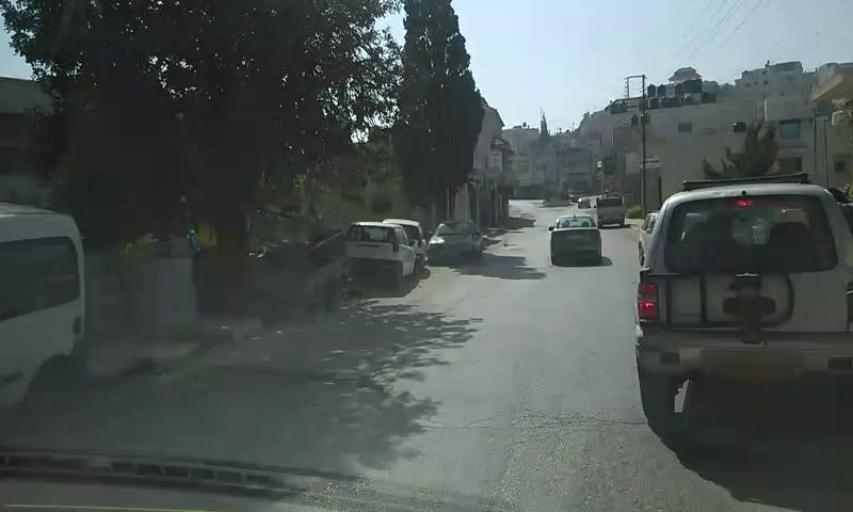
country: PS
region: West Bank
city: At Taybah
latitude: 31.9568
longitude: 35.2983
